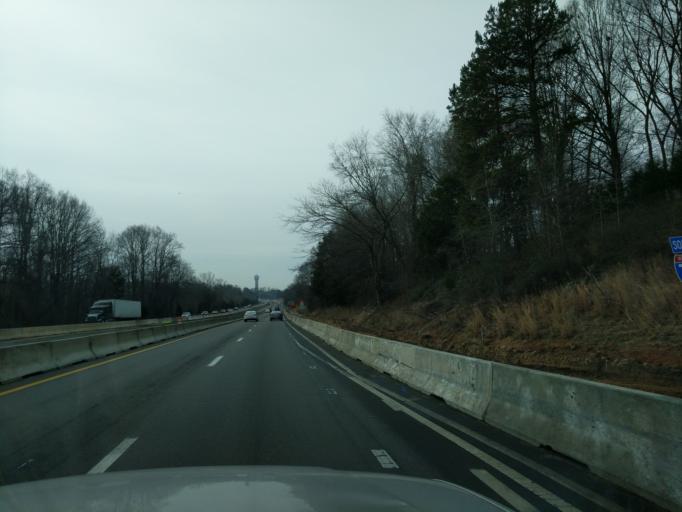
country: US
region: North Carolina
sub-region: Iredell County
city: Mooresville
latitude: 35.5732
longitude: -80.8562
